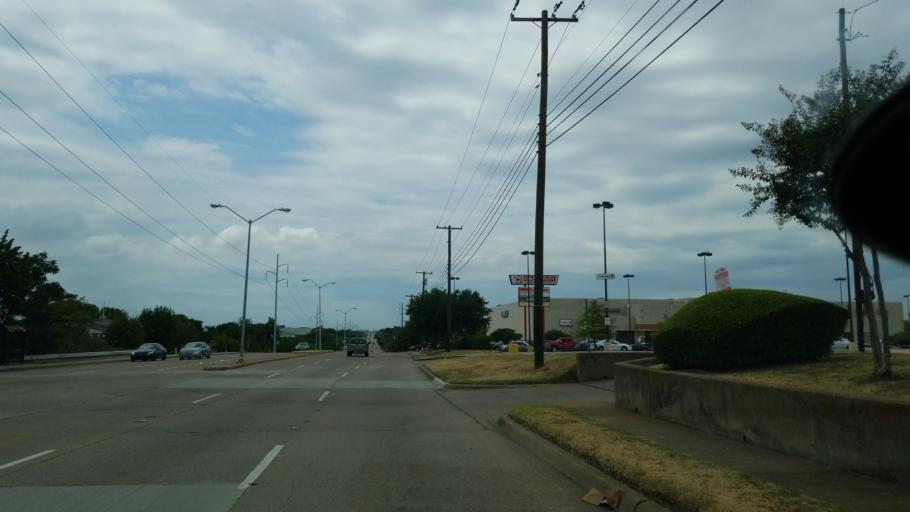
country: US
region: Texas
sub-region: Dallas County
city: Duncanville
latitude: 32.6622
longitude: -96.8414
